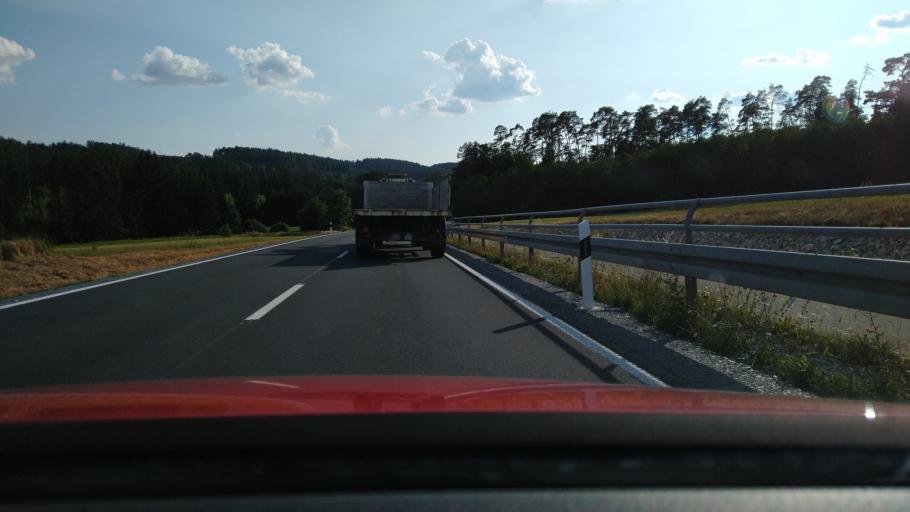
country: DE
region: Bavaria
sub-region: Upper Franconia
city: Mistelgau
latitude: 49.9248
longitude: 11.4392
